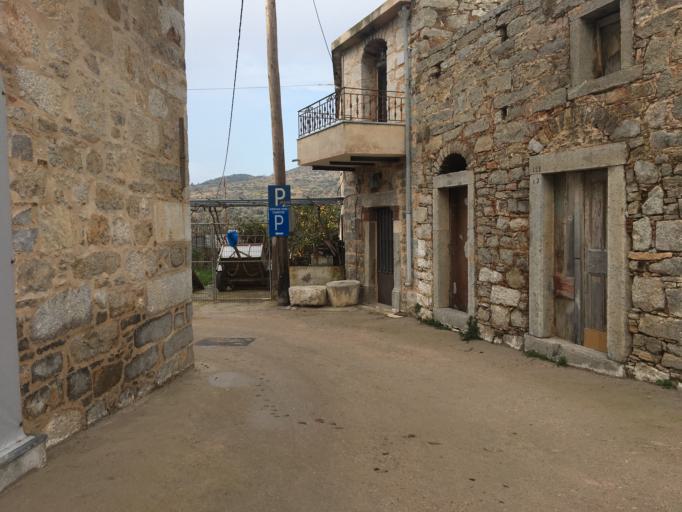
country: GR
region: North Aegean
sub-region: Chios
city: Thymiana
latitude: 38.2479
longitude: 25.9421
